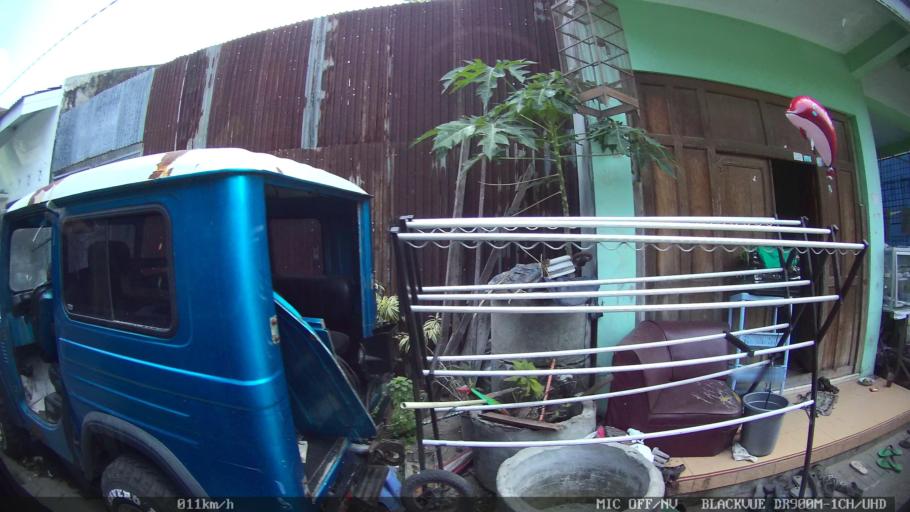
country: ID
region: Daerah Istimewa Yogyakarta
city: Yogyakarta
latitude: -7.8141
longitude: 110.3991
